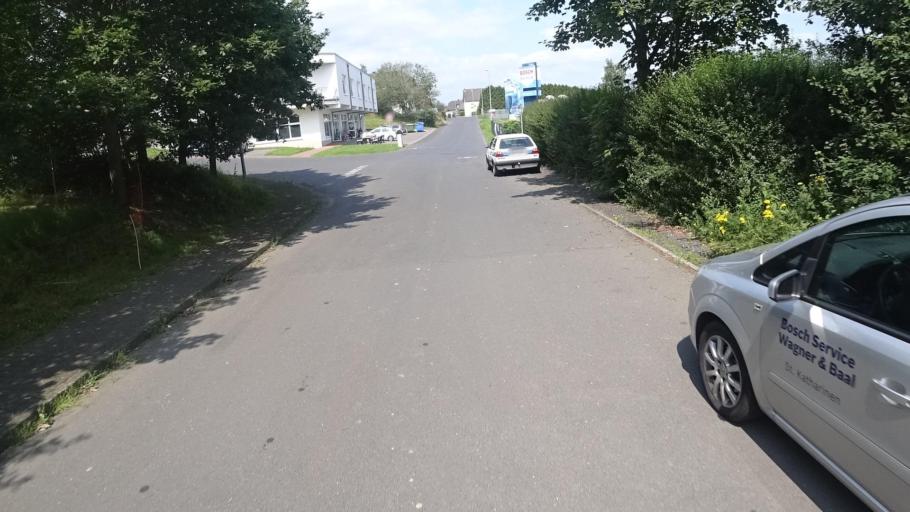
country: DE
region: Rheinland-Pfalz
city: Sankt Katharinen
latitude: 50.5958
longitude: 7.3641
